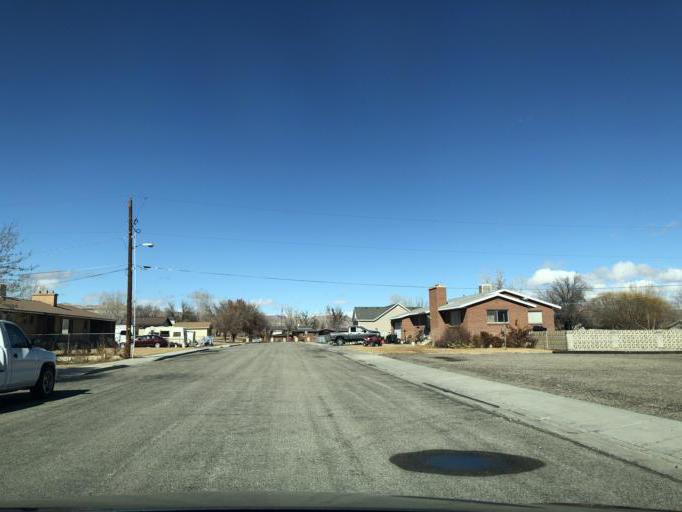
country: US
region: Utah
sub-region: Carbon County
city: East Carbon City
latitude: 38.9976
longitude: -110.1610
